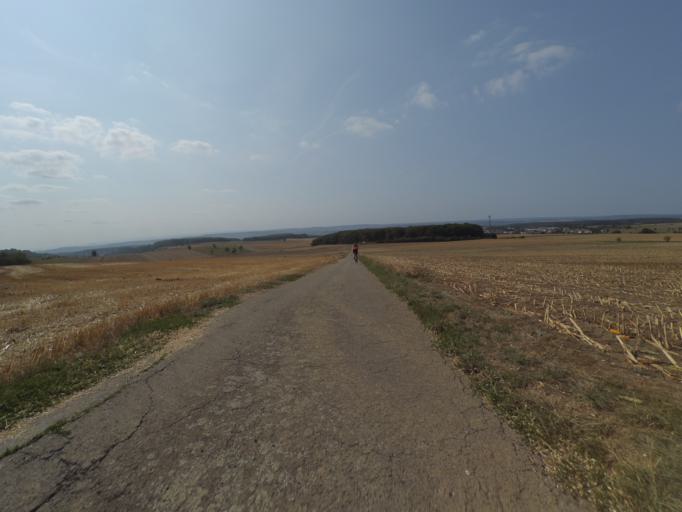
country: DE
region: Rheinland-Pfalz
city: Kirf
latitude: 49.5490
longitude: 6.4626
